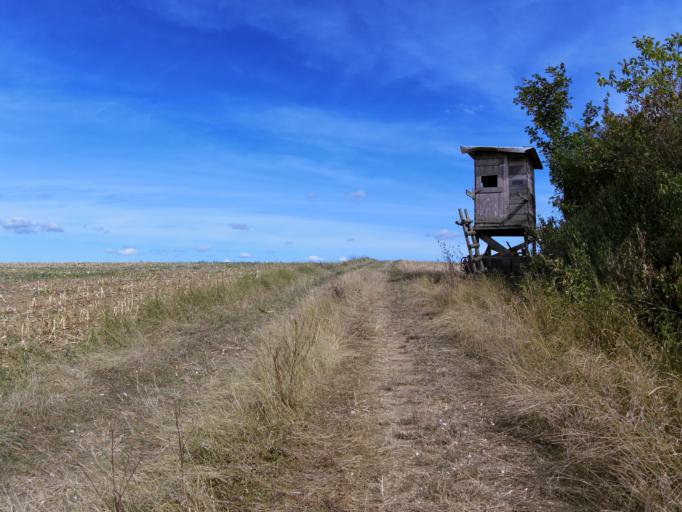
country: DE
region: Bavaria
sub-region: Regierungsbezirk Unterfranken
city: Rimpar
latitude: 49.8448
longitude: 9.9355
